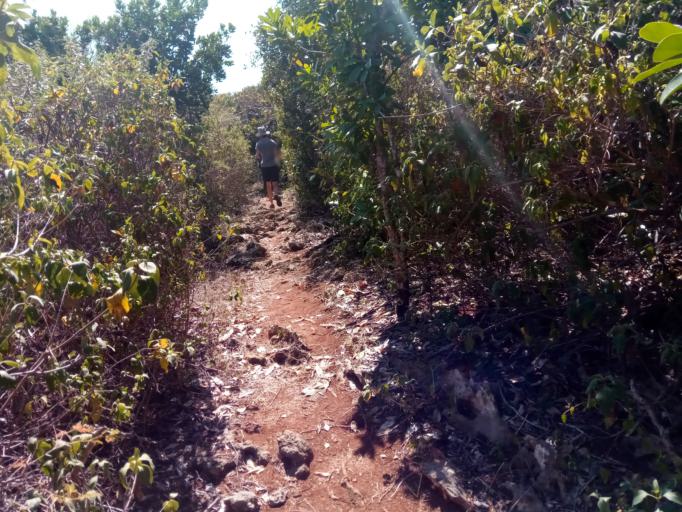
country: GP
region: Guadeloupe
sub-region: Guadeloupe
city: Saint-Francois
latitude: 16.2668
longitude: -61.2342
